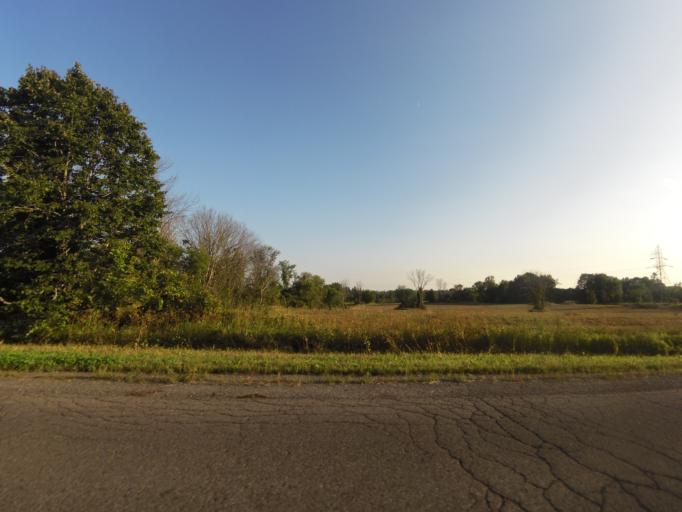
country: CA
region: Ontario
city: Clarence-Rockland
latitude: 45.4988
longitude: -75.4165
